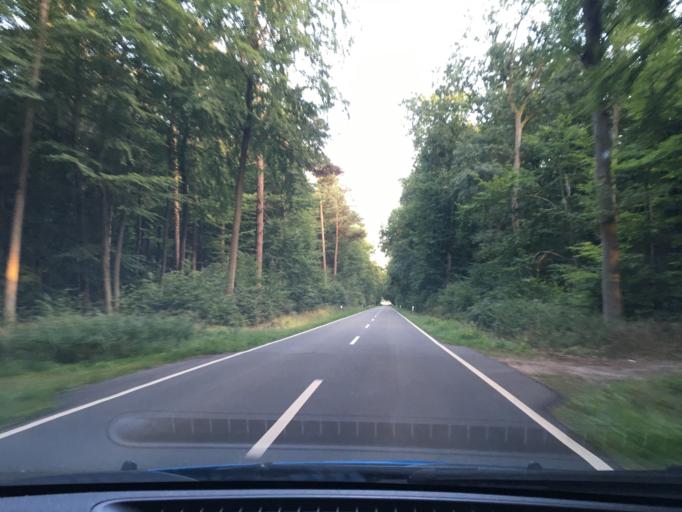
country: DE
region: Lower Saxony
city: Tosterglope
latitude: 53.2276
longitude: 10.8042
